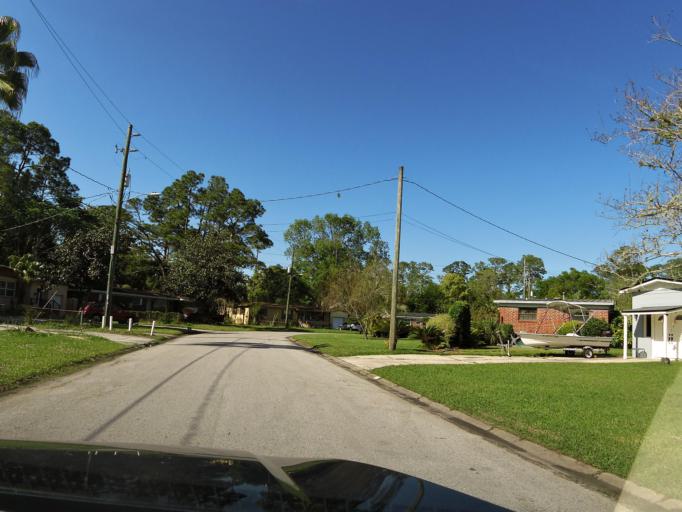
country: US
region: Florida
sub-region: Duval County
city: Jacksonville
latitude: 30.2844
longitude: -81.5956
